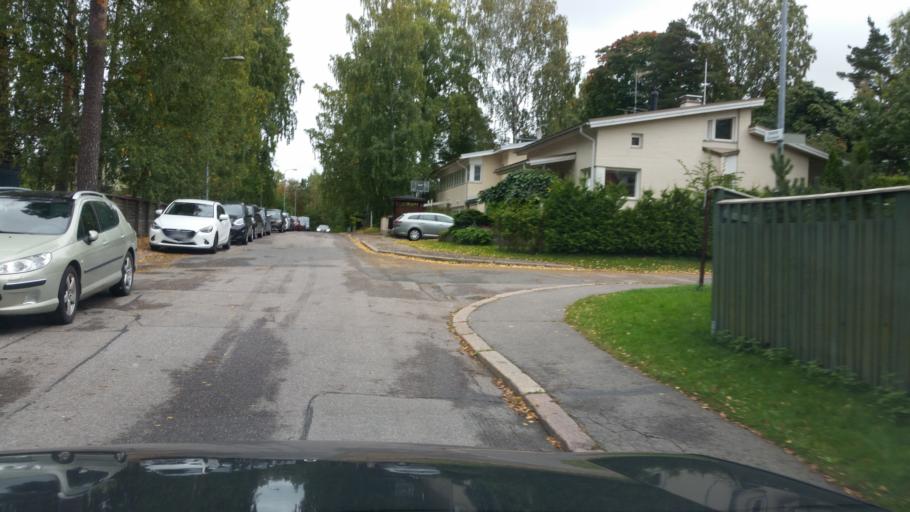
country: FI
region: Uusimaa
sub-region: Helsinki
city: Helsinki
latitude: 60.2451
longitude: 24.9359
